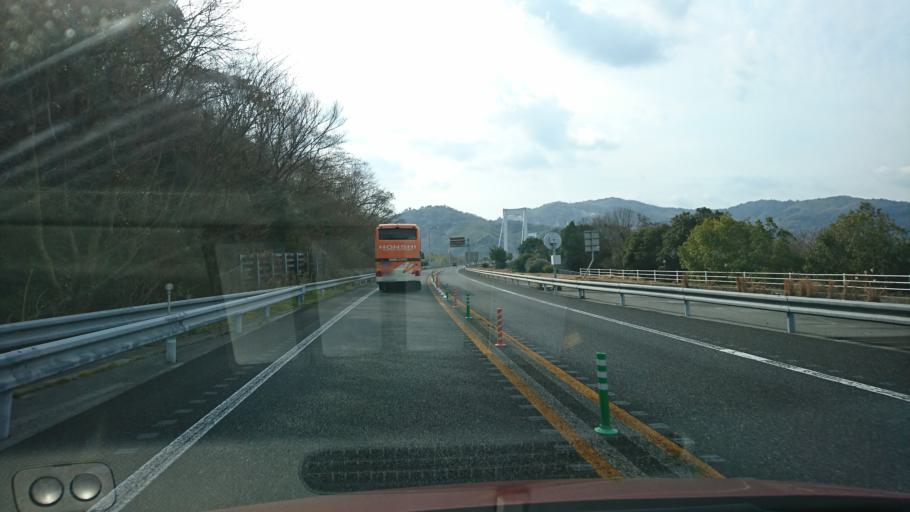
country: JP
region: Hiroshima
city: Innoshima
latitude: 34.1992
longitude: 133.0784
